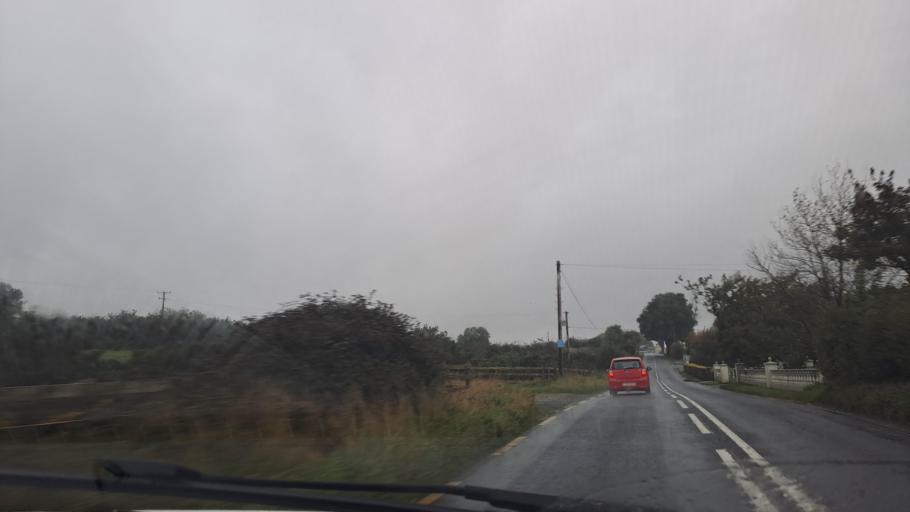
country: IE
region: Leinster
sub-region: Lu
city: Ardee
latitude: 53.9723
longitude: -6.5454
